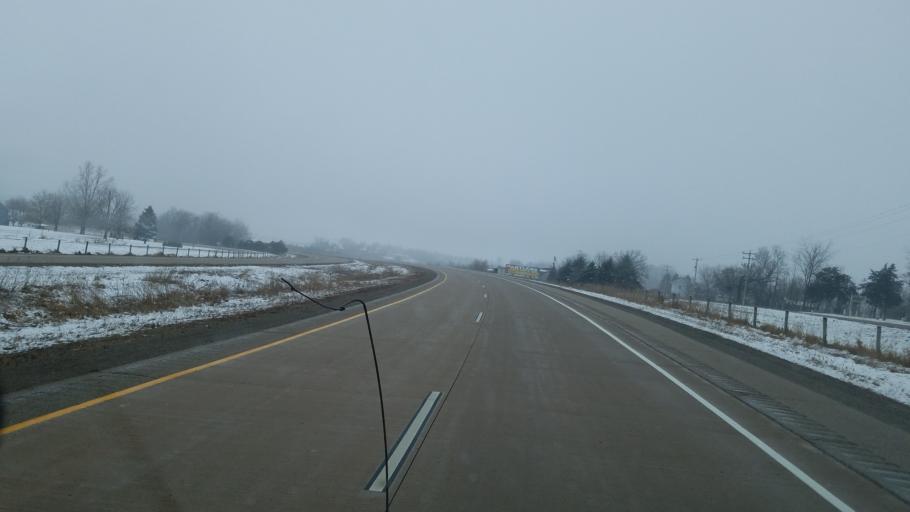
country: US
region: Wisconsin
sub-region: Winnebago County
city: Winneconne
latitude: 44.1239
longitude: -88.6543
